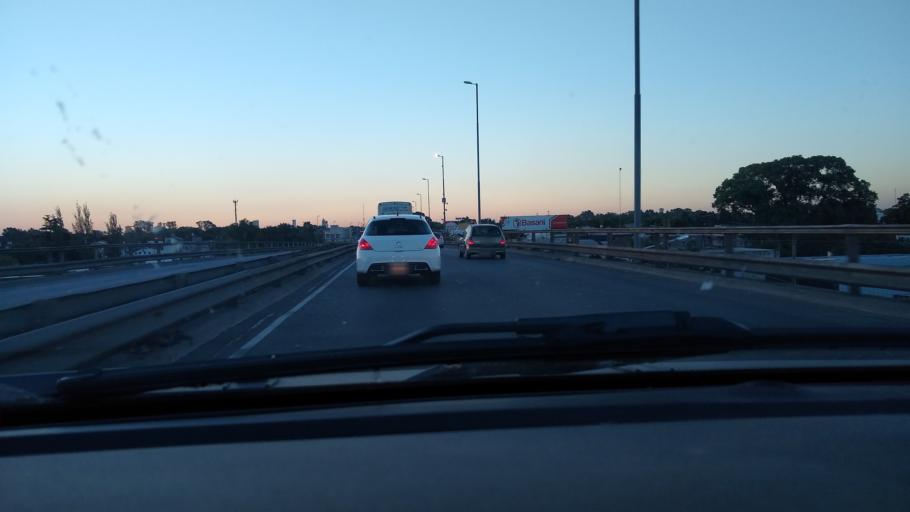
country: AR
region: Buenos Aires
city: San Justo
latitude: -34.7122
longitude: -58.5253
